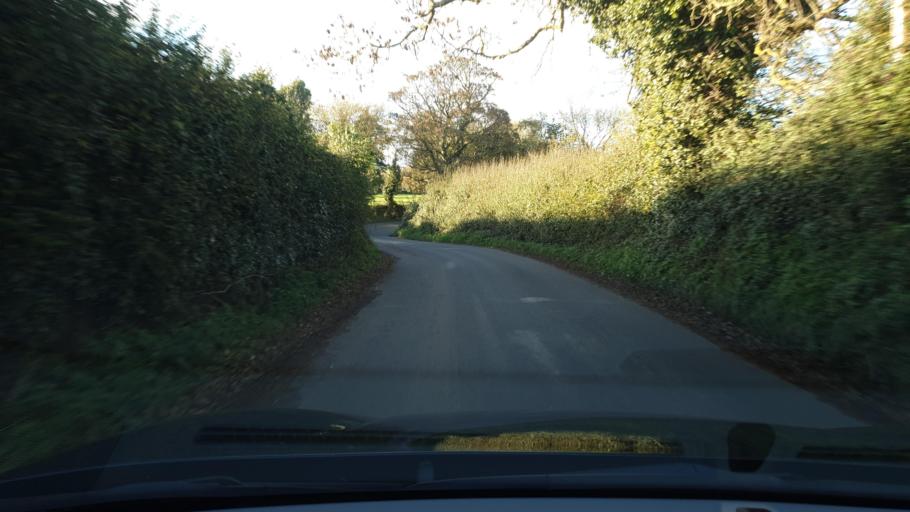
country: IE
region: Leinster
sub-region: An Mhi
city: Stamullin
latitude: 53.6197
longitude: -6.2589
